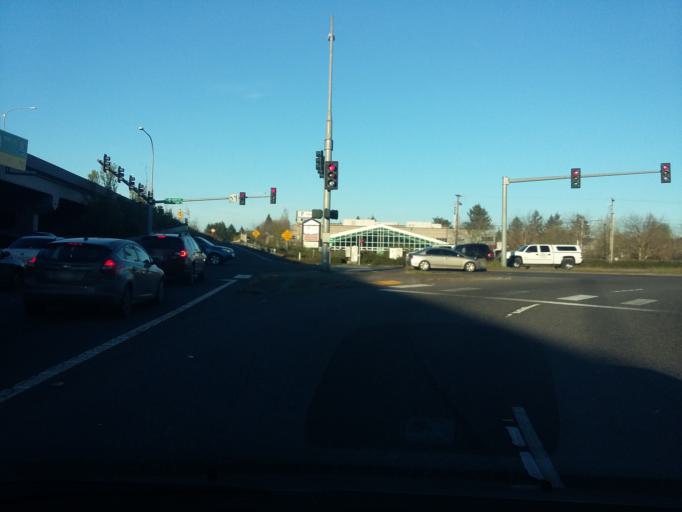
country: US
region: Washington
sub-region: Clark County
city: Orchards
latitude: 45.6612
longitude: -122.5593
